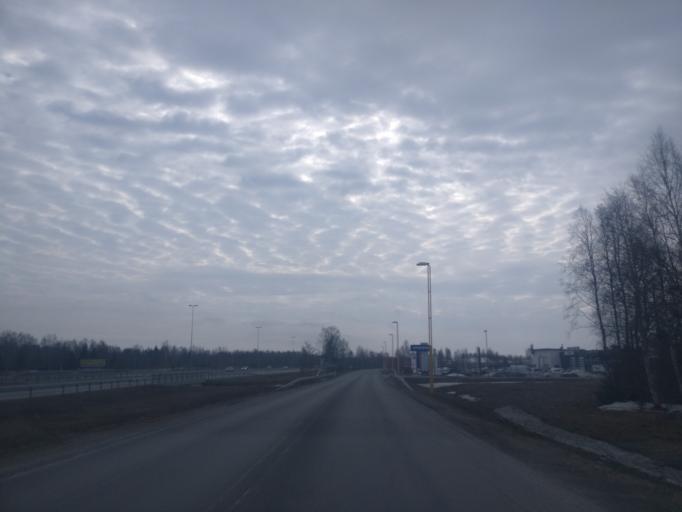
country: FI
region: Lapland
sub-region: Kemi-Tornio
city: Kemi
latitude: 65.7422
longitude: 24.5844
